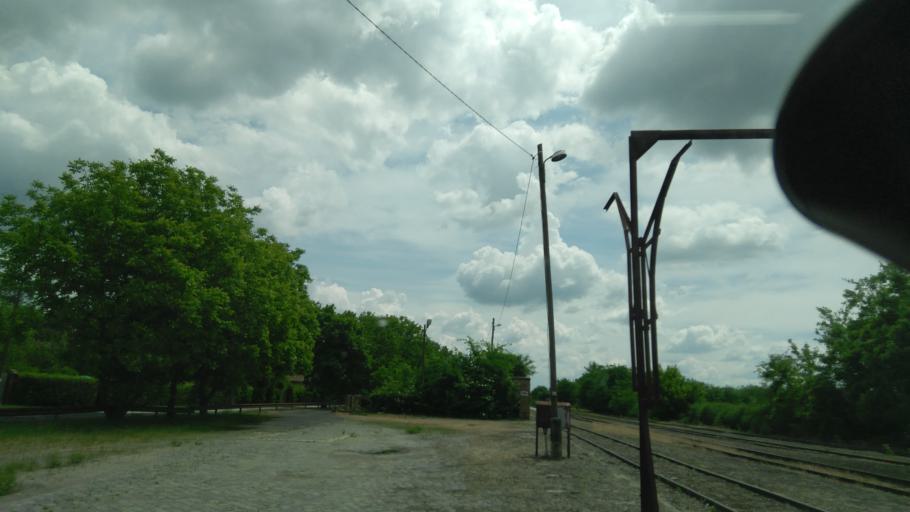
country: HU
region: Bekes
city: Totkomlos
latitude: 46.4107
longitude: 20.7265
